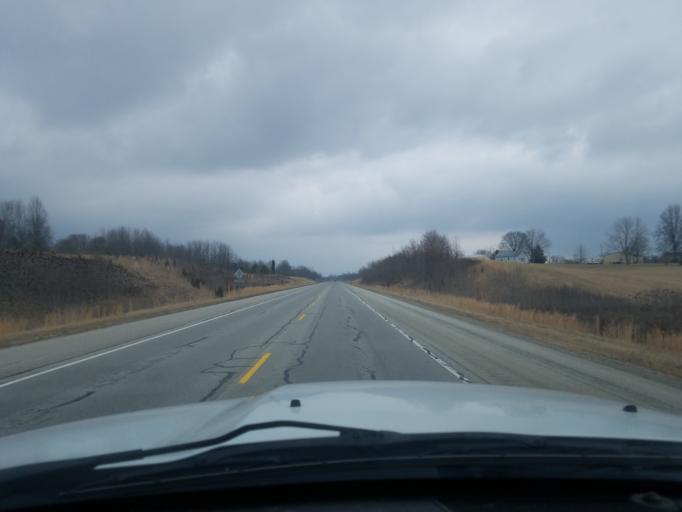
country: US
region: Indiana
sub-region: Perry County
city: Tell City
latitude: 37.9901
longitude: -86.7103
